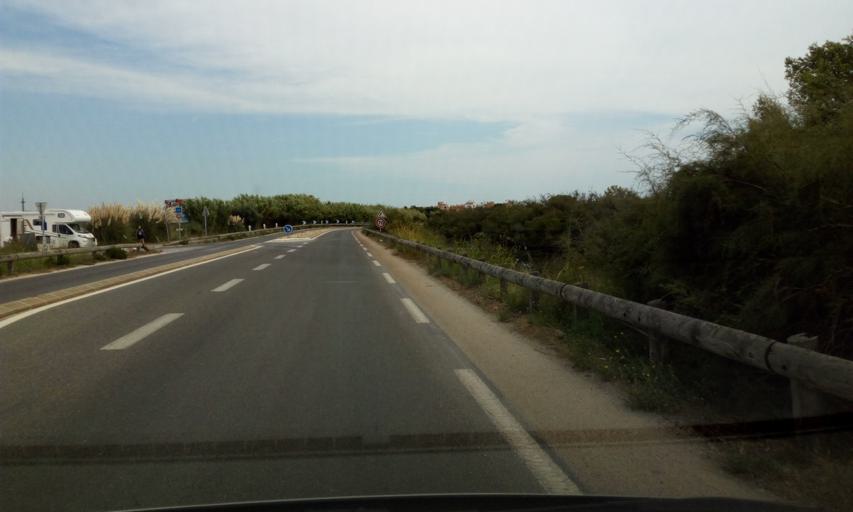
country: FR
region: Provence-Alpes-Cote d'Azur
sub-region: Departement du Var
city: Hyeres
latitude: 43.0819
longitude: 6.1422
